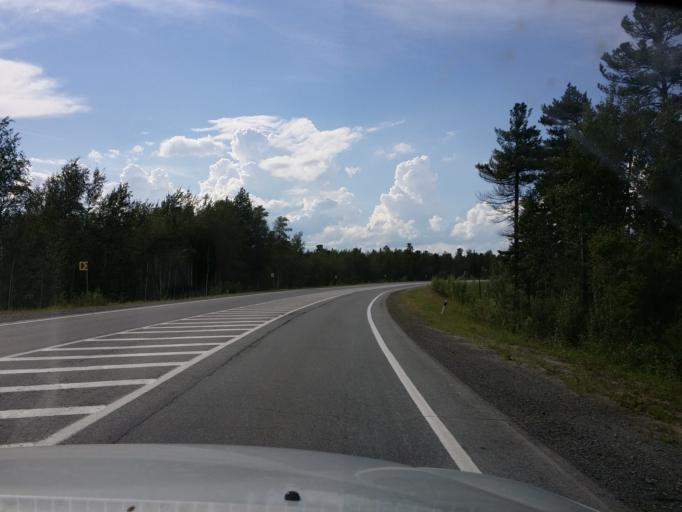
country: RU
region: Khanty-Mansiyskiy Avtonomnyy Okrug
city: Megion
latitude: 61.1001
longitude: 75.8615
